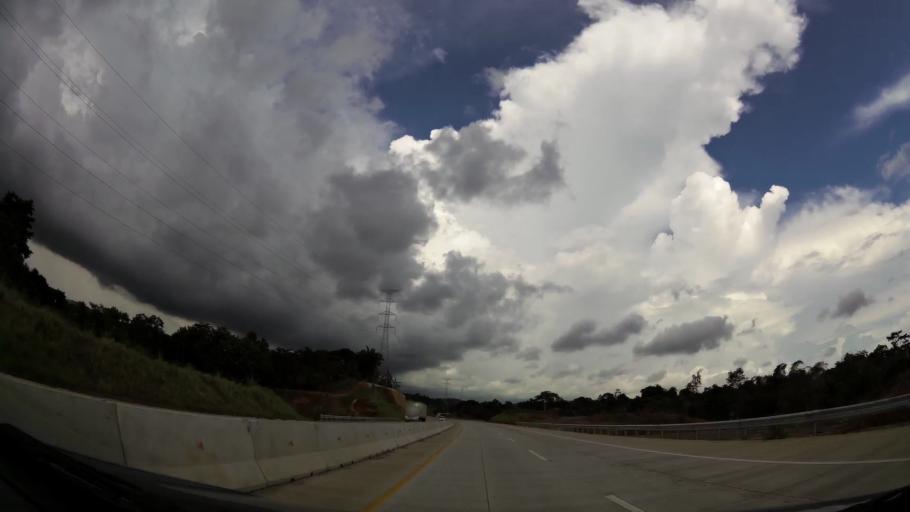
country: PA
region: Panama
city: Tocumen
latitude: 9.1045
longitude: -79.4116
